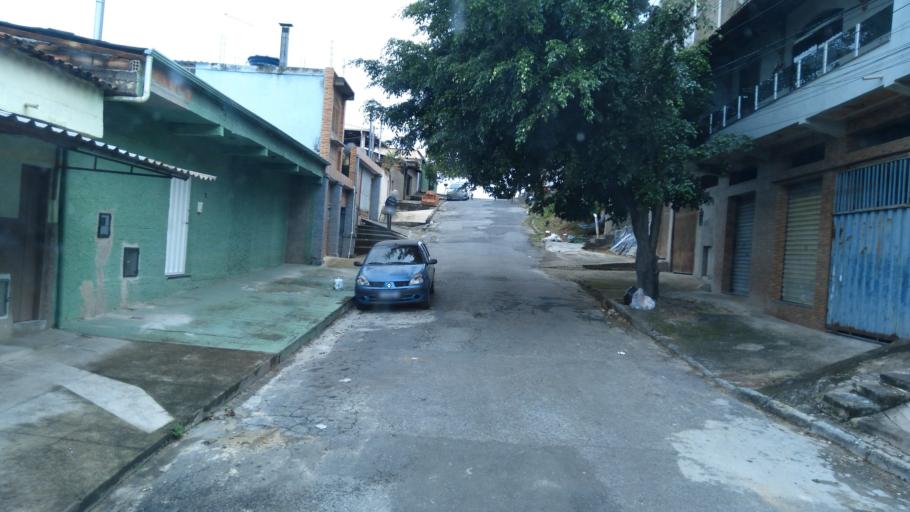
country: BR
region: Minas Gerais
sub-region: Belo Horizonte
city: Belo Horizonte
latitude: -19.8676
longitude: -43.9003
